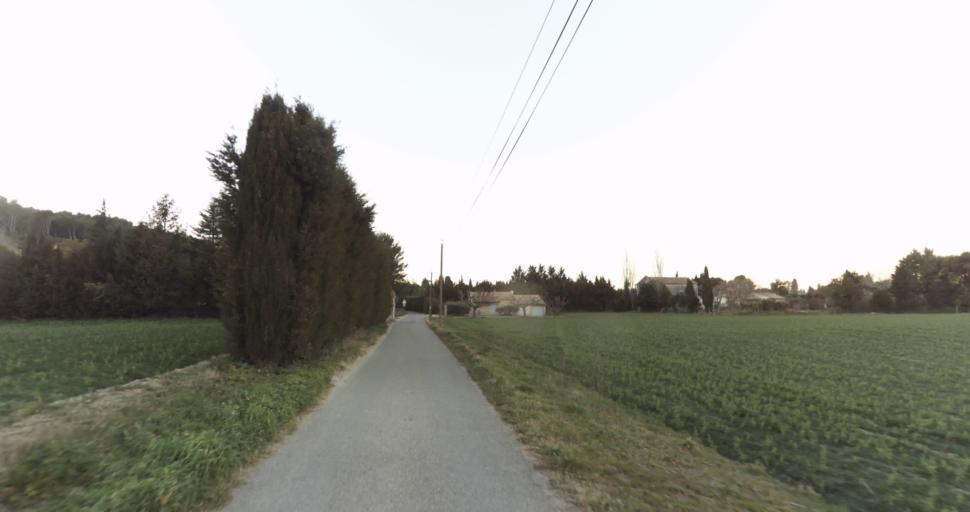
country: FR
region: Provence-Alpes-Cote d'Azur
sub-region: Departement des Bouches-du-Rhone
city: Barbentane
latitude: 43.8954
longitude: 4.7656
